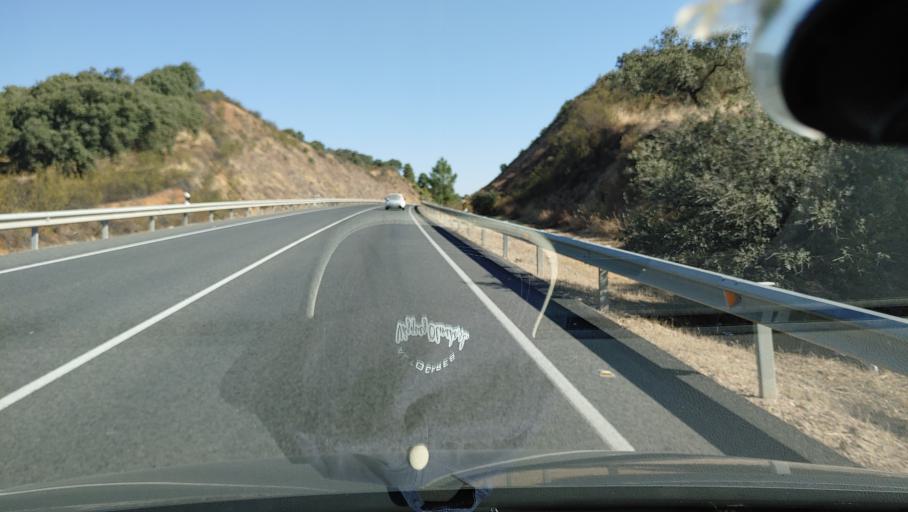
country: ES
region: Andalusia
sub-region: Province of Cordoba
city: Obejo
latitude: 38.0260
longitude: -4.8102
